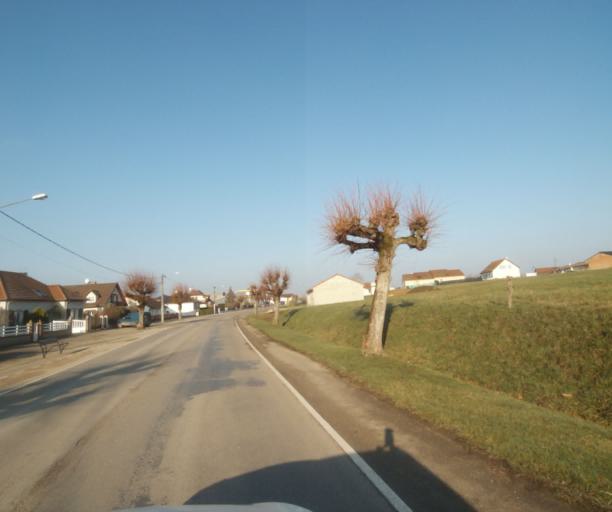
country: FR
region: Champagne-Ardenne
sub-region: Departement de la Haute-Marne
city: Montier-en-Der
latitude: 48.4840
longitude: 4.7621
